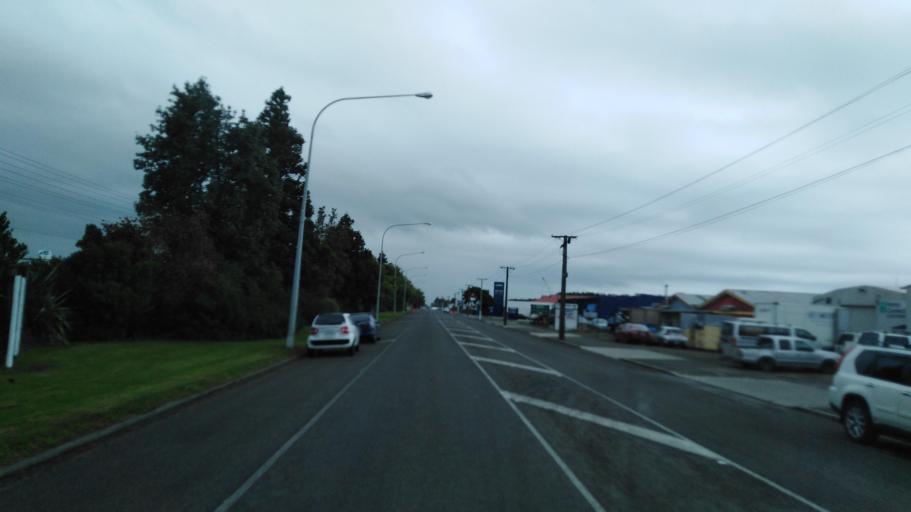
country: NZ
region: Manawatu-Wanganui
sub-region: Horowhenua District
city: Levin
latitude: -40.6342
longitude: 175.2747
